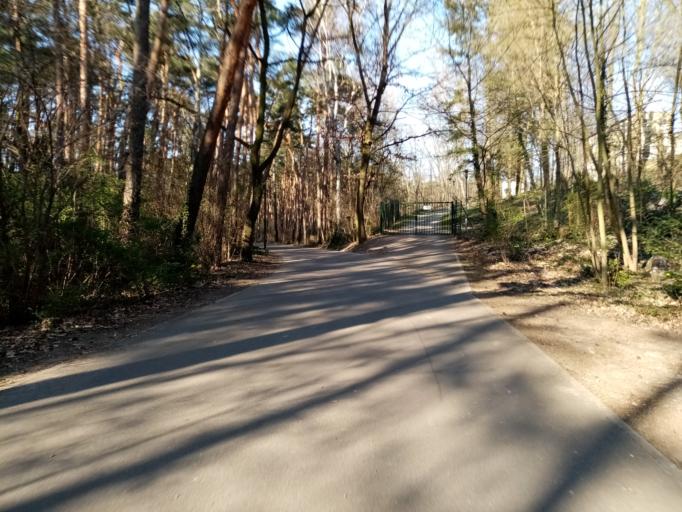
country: DE
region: Berlin
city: Oberschoneweide
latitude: 52.4621
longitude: 13.5435
